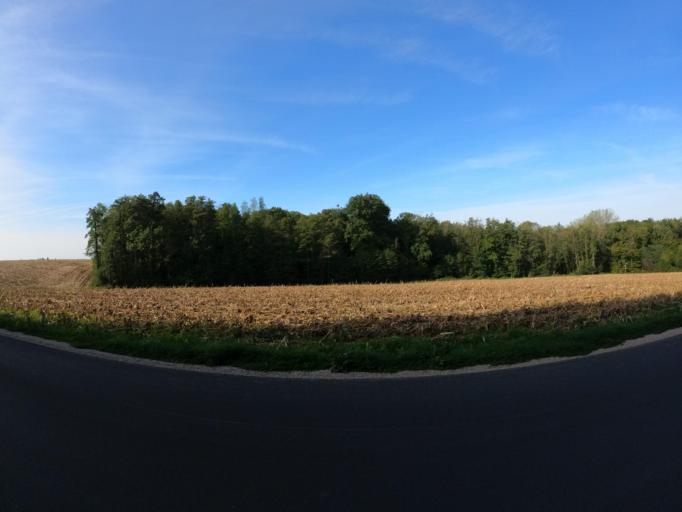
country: FR
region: Franche-Comte
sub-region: Departement du Jura
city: Montmorot
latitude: 46.7194
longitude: 5.5167
